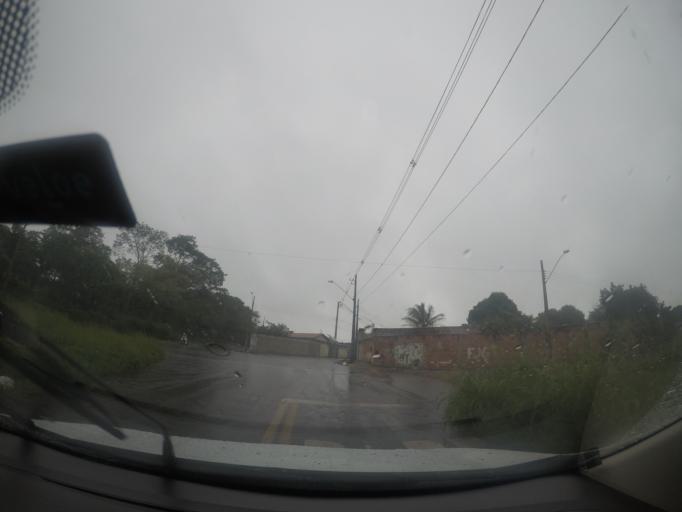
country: BR
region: Goias
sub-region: Goiania
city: Goiania
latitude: -16.5901
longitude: -49.3428
